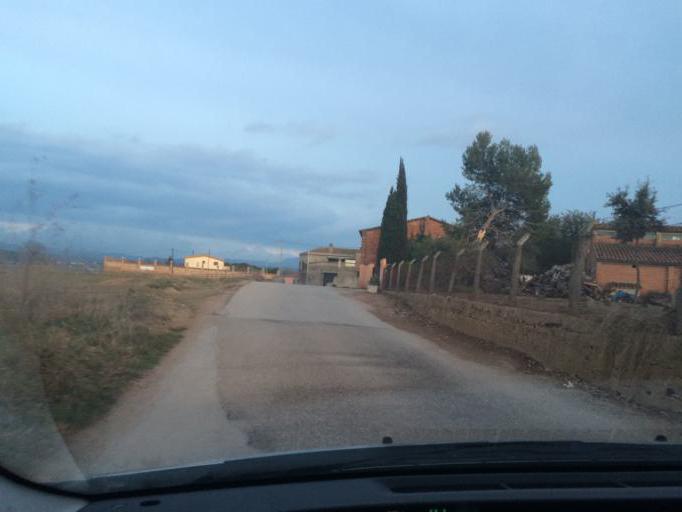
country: ES
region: Catalonia
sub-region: Provincia de Barcelona
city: Sant Fruitos de Bages
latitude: 41.7487
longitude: 1.8464
